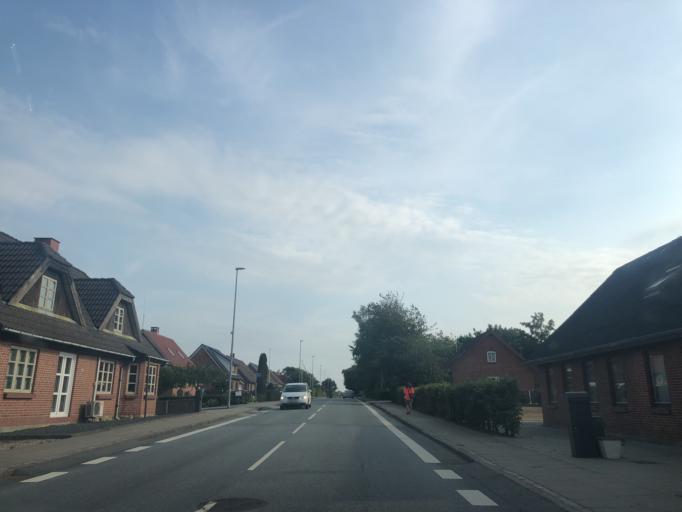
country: DK
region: Central Jutland
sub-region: Skive Kommune
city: Skive
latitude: 56.6207
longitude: 8.8802
